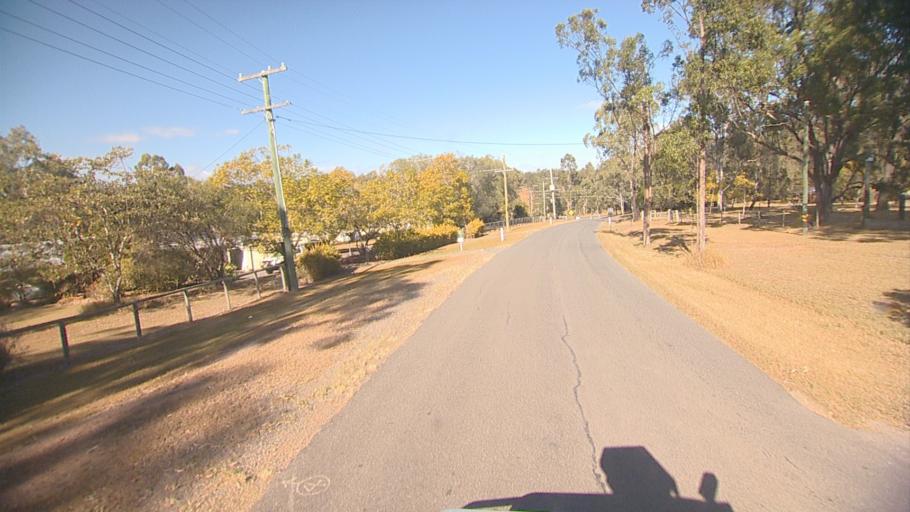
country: AU
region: Queensland
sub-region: Logan
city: Cedar Vale
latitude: -27.8607
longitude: 152.9905
